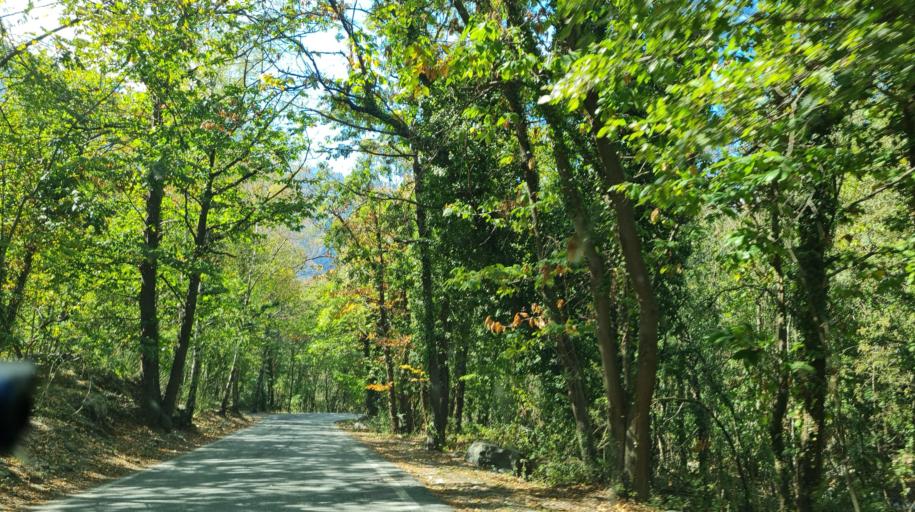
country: IT
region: Aosta Valley
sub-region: Valle d'Aosta
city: Arnad
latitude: 45.6387
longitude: 7.7339
